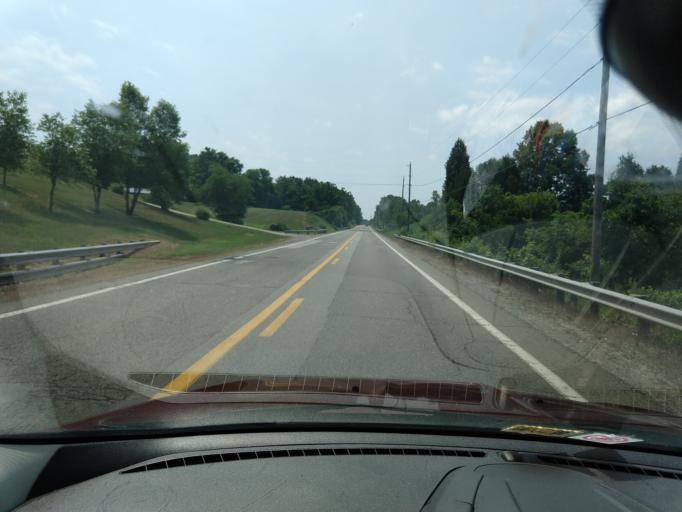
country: US
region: West Virginia
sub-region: Jackson County
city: Ripley
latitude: 38.8520
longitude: -81.8008
